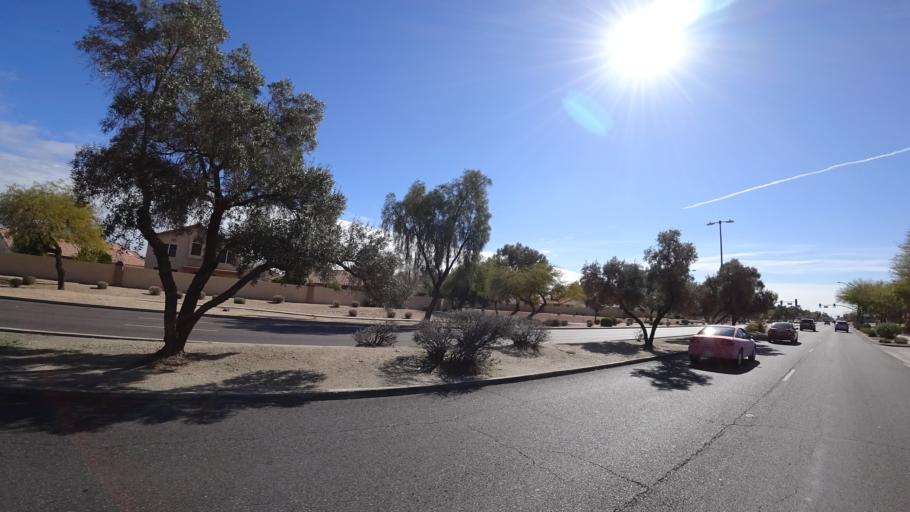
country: US
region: Arizona
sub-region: Maricopa County
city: Glendale
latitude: 33.5797
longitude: -112.1863
